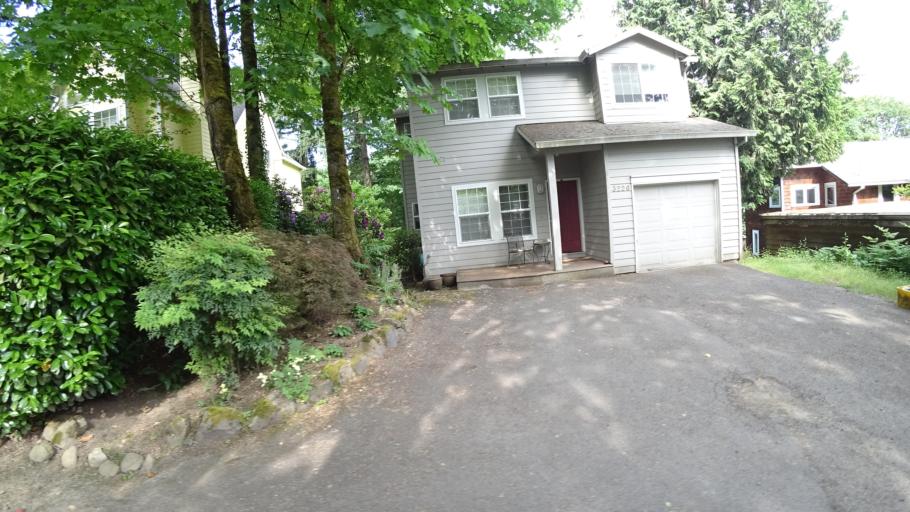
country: US
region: Oregon
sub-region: Multnomah County
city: Portland
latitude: 45.5057
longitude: -122.7098
